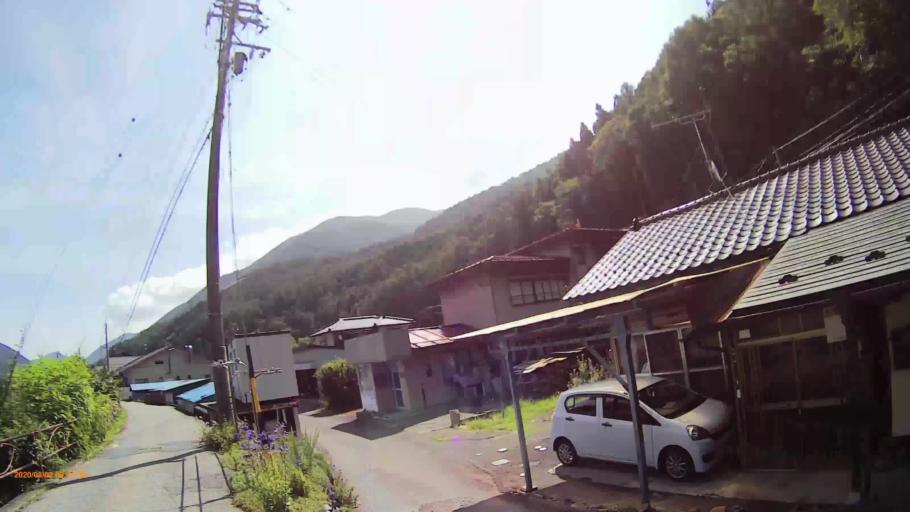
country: JP
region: Nagano
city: Tatsuno
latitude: 35.9723
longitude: 137.8219
